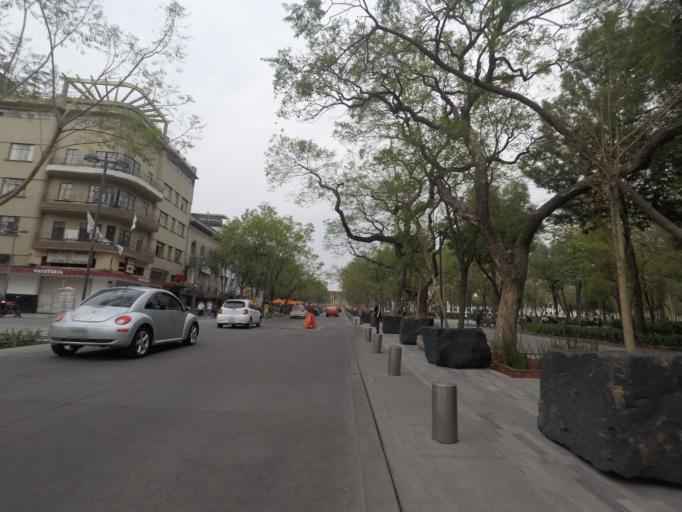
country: MX
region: Mexico City
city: Cuauhtemoc
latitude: 19.4357
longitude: -99.1461
